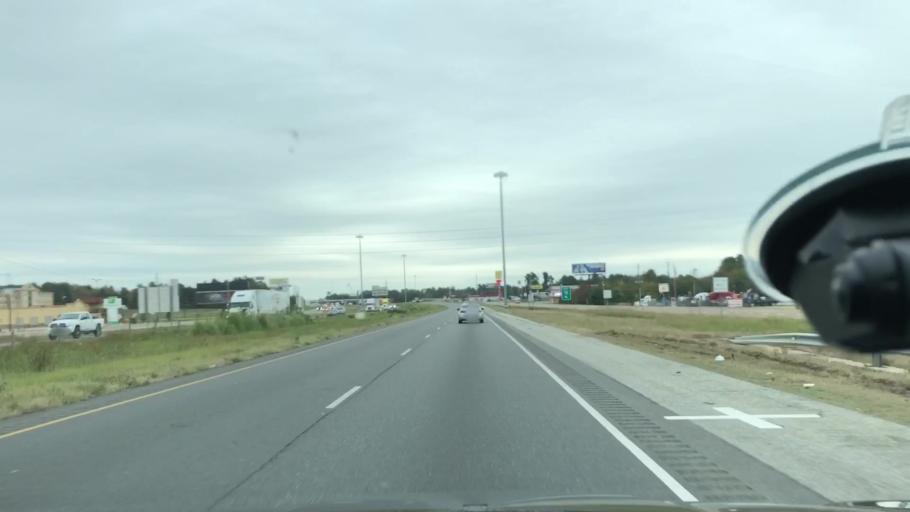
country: US
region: Arkansas
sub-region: Miller County
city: Texarkana
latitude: 33.4702
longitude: -94.0390
